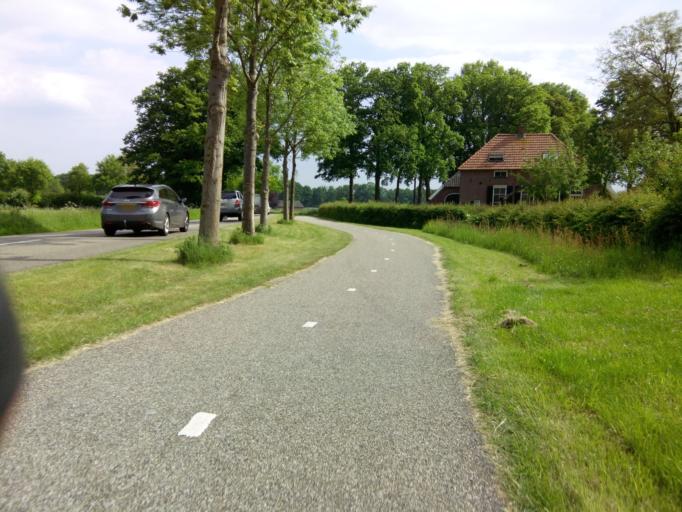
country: NL
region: Gelderland
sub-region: Berkelland
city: Borculo
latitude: 52.1010
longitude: 6.5253
